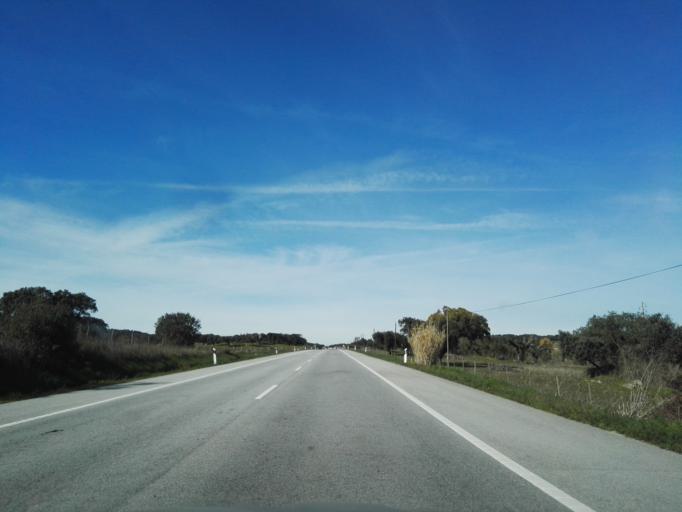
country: PT
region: Portalegre
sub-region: Arronches
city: Arronches
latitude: 39.1650
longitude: -7.3262
